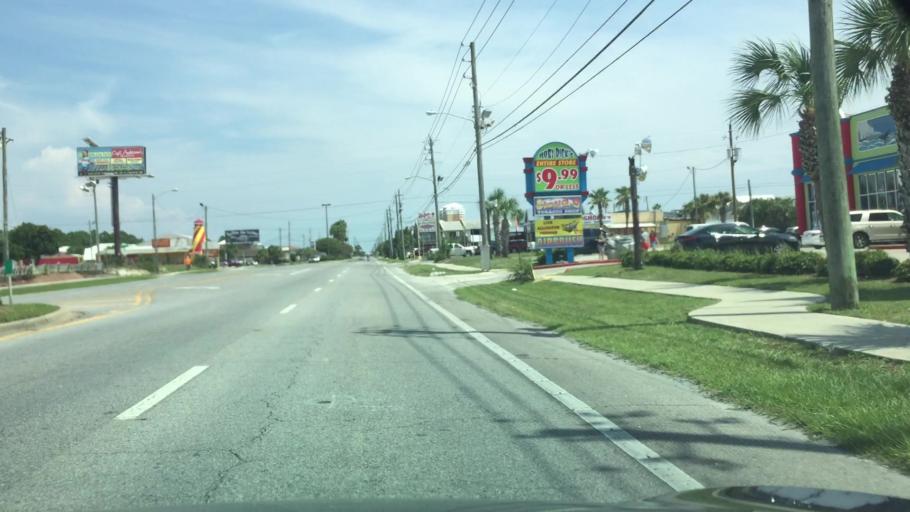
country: US
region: Florida
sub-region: Bay County
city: Panama City Beach
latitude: 30.1667
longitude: -85.7879
